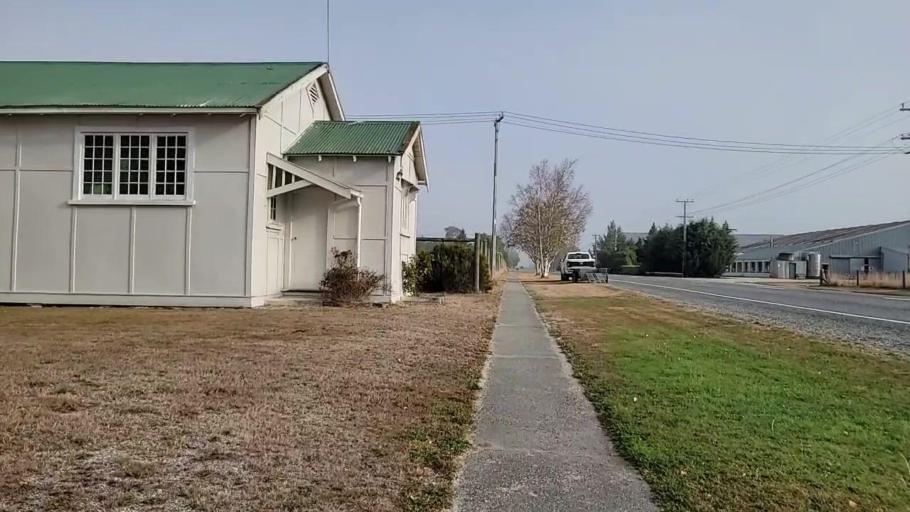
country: NZ
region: Southland
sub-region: Gore District
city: Gore
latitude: -45.6373
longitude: 169.3676
